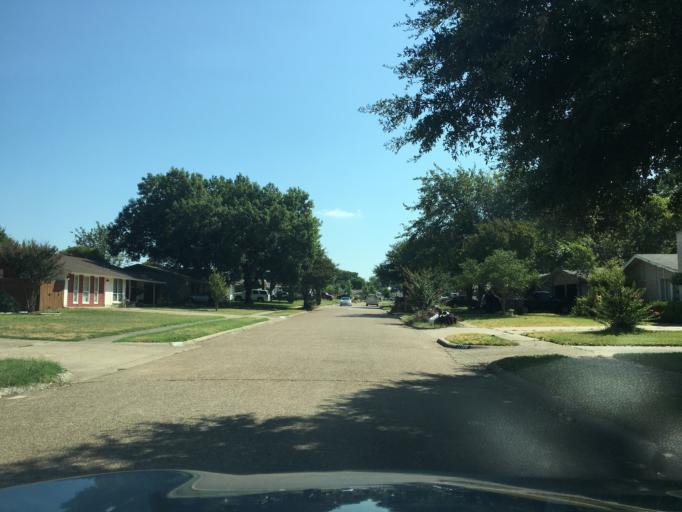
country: US
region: Texas
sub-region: Dallas County
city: Garland
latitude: 32.8619
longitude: -96.6859
